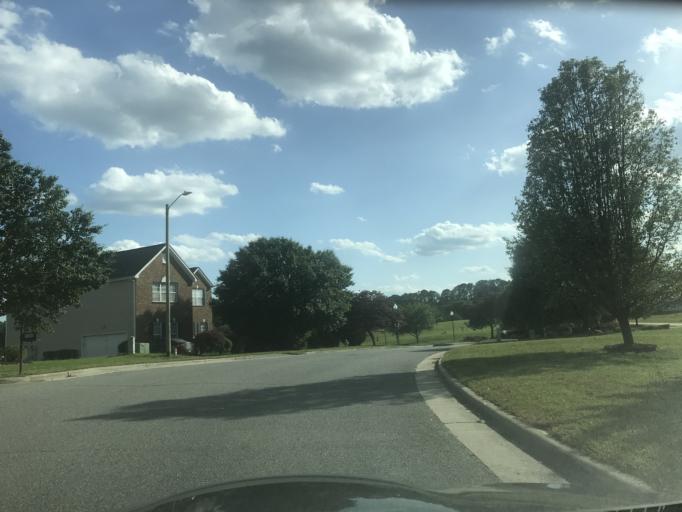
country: US
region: North Carolina
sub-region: Wake County
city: Knightdale
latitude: 35.8354
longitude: -78.5485
